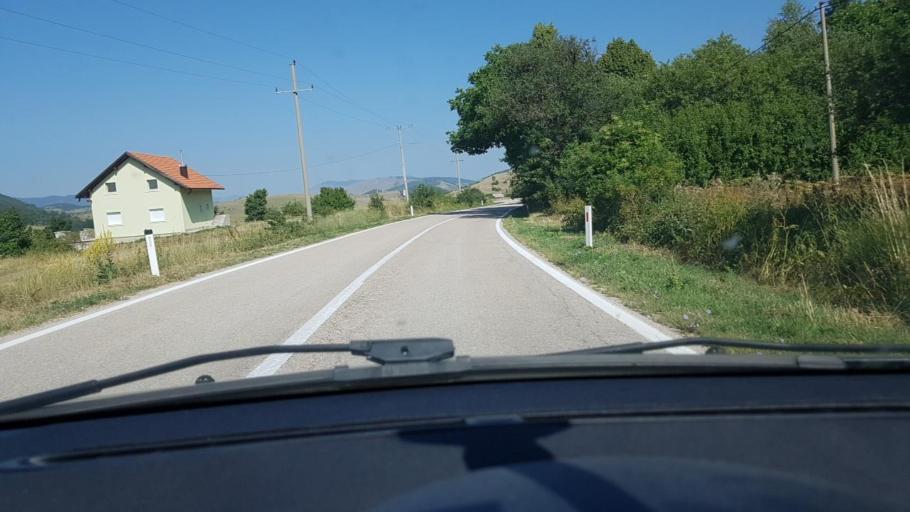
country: BA
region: Federation of Bosnia and Herzegovina
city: Bosansko Grahovo
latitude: 44.1217
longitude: 16.5310
